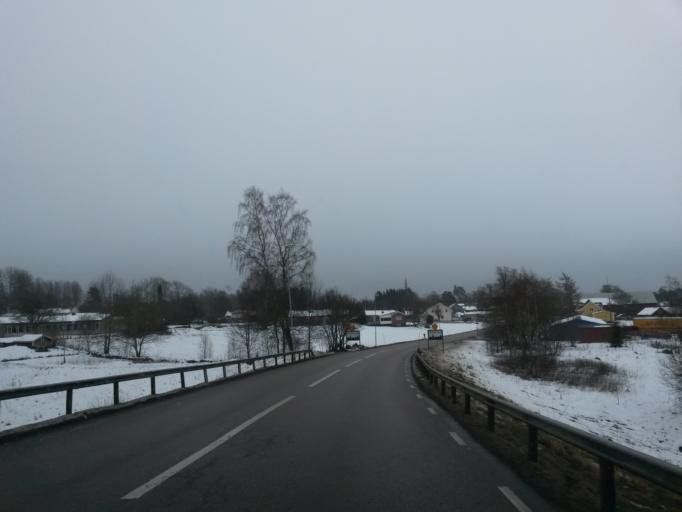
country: SE
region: Vaestra Goetaland
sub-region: Ulricehamns Kommun
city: Ulricehamn
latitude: 57.9016
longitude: 13.3444
